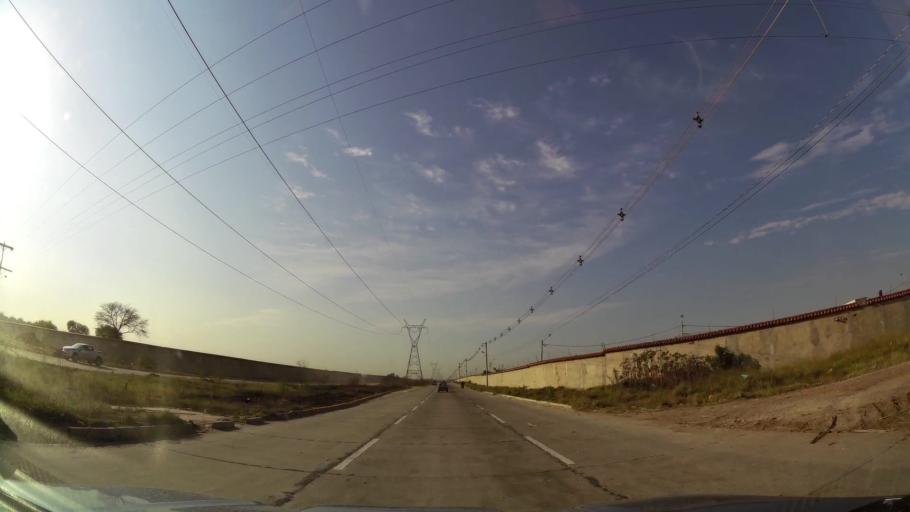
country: BO
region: Santa Cruz
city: Santa Cruz de la Sierra
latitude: -17.6796
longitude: -63.1537
